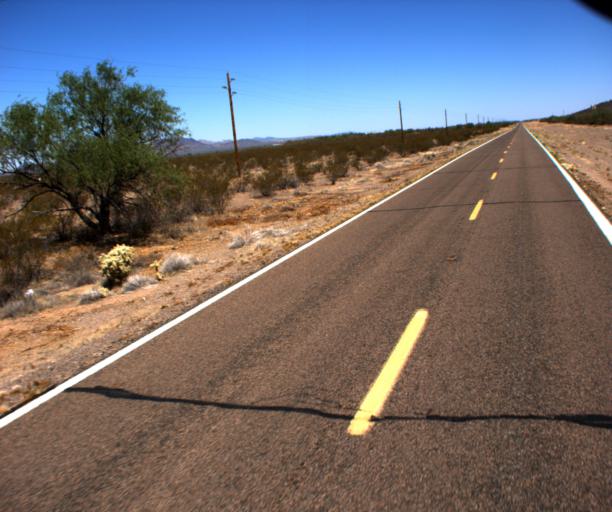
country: US
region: Arizona
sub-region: Pima County
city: Ajo
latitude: 32.2492
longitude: -112.7301
